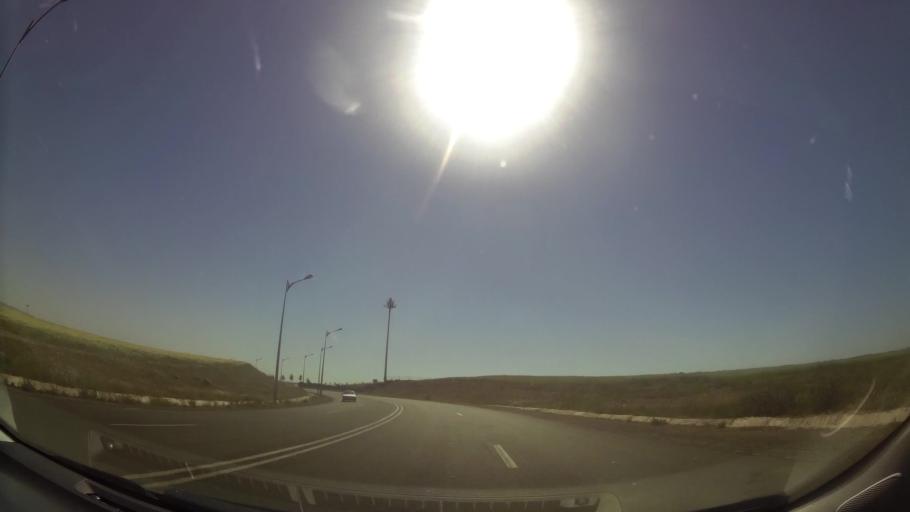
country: MA
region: Oriental
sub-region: Oujda-Angad
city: Oujda
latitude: 34.7403
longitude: -1.9170
